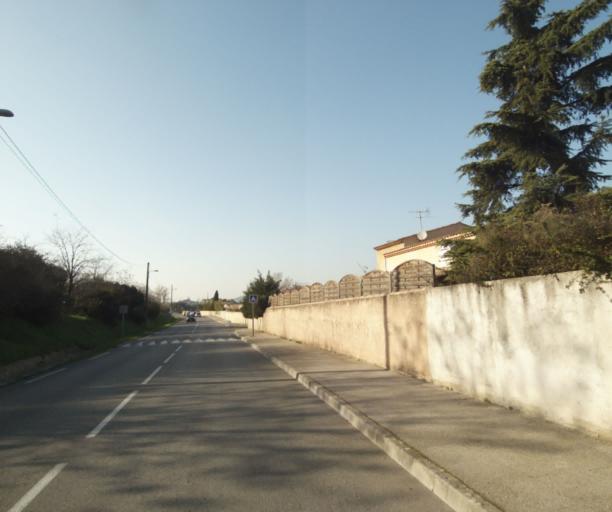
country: FR
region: Provence-Alpes-Cote d'Azur
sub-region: Departement des Bouches-du-Rhone
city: Les Pennes-Mirabeau
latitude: 43.4142
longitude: 5.3000
